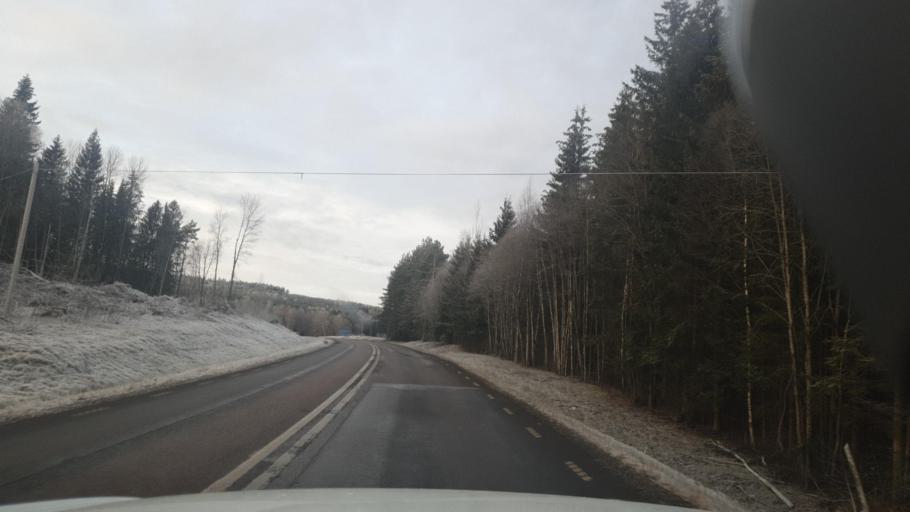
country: SE
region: Vaermland
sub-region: Eda Kommun
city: Amotfors
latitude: 59.6810
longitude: 12.3976
